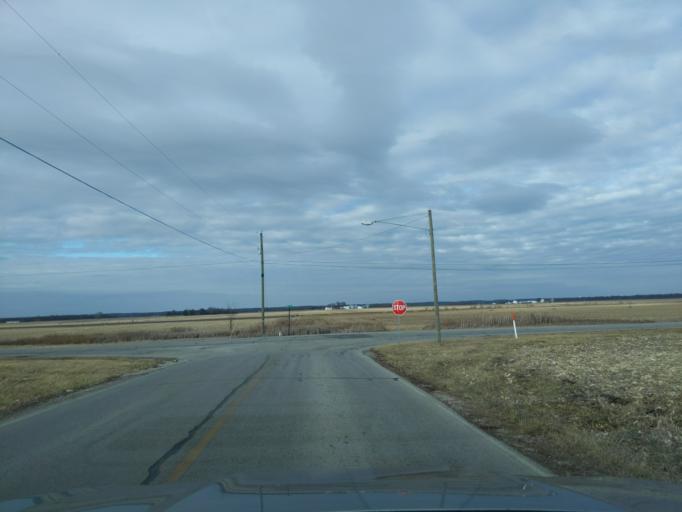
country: US
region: Indiana
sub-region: Tippecanoe County
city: Shadeland
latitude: 40.3590
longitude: -86.9754
